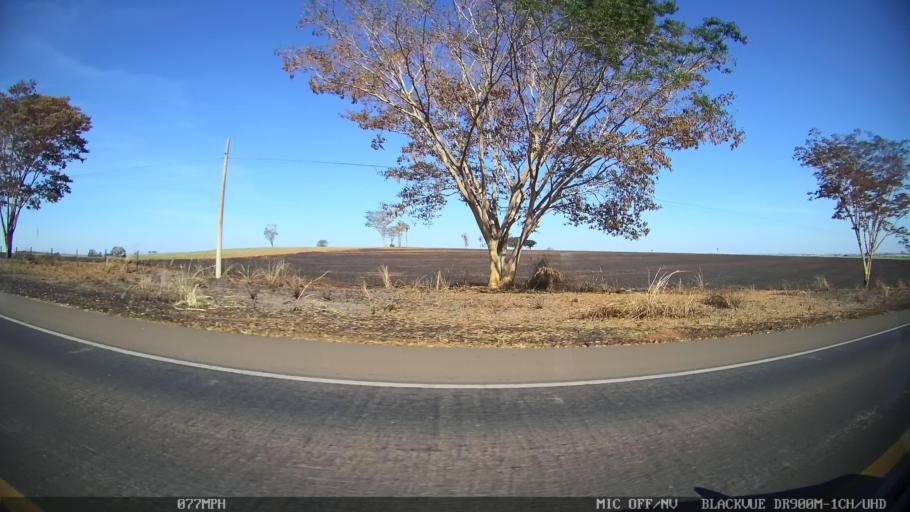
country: BR
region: Sao Paulo
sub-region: Olimpia
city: Olimpia
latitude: -20.6630
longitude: -48.8630
